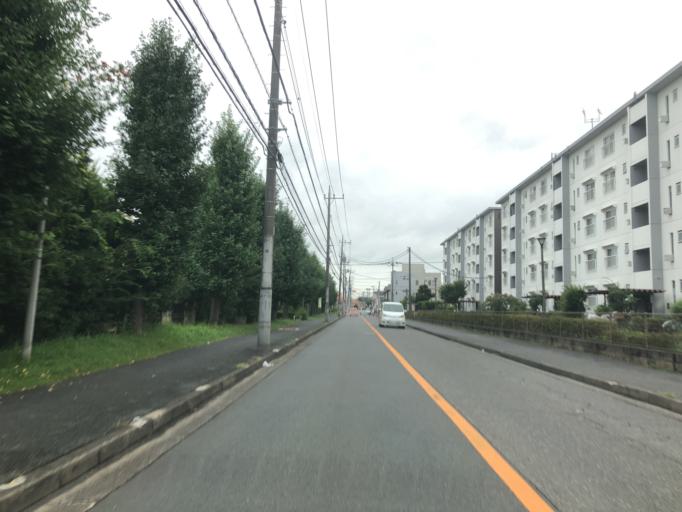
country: JP
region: Saitama
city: Sakado
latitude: 35.9765
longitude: 139.3951
